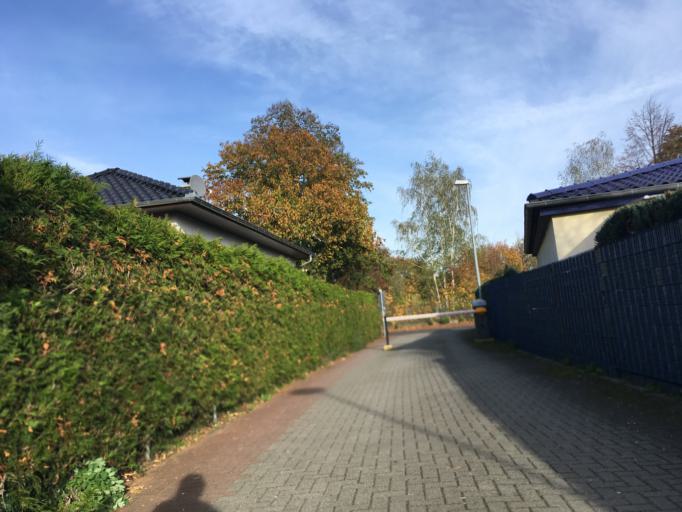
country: DE
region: Berlin
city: Buchholz
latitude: 52.5977
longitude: 13.4298
